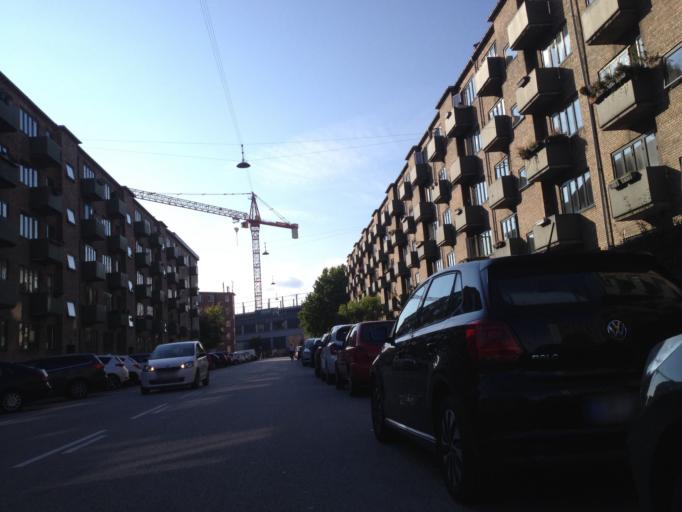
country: DK
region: Capital Region
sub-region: Kobenhavn
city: Christianshavn
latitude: 55.6624
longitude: 12.6087
